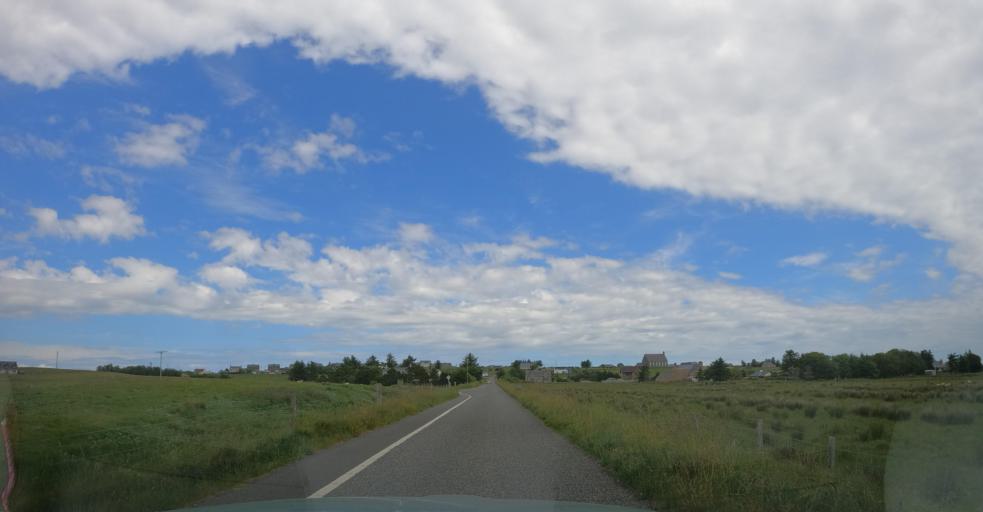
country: GB
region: Scotland
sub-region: Eilean Siar
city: Isle of Lewis
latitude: 58.2727
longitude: -6.2969
